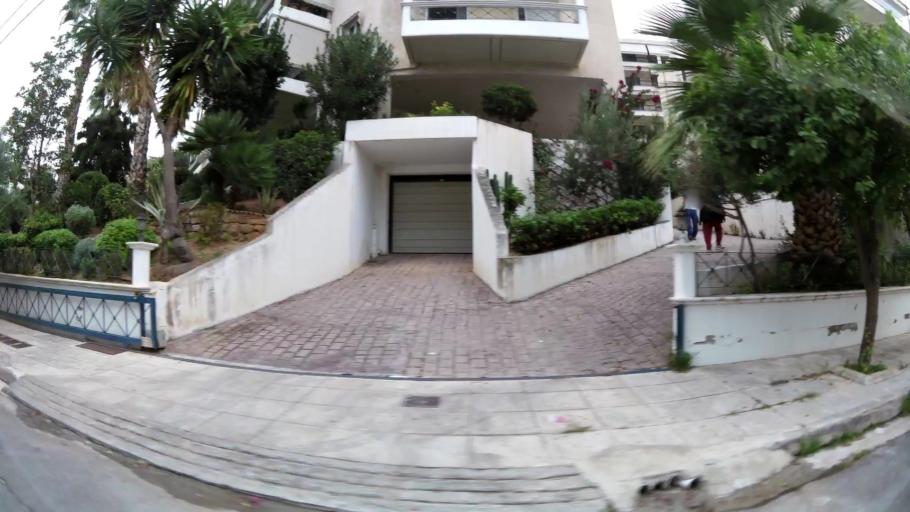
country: GR
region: Attica
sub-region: Nomarchia Athinas
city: Alimos
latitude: 37.9083
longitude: 23.7280
